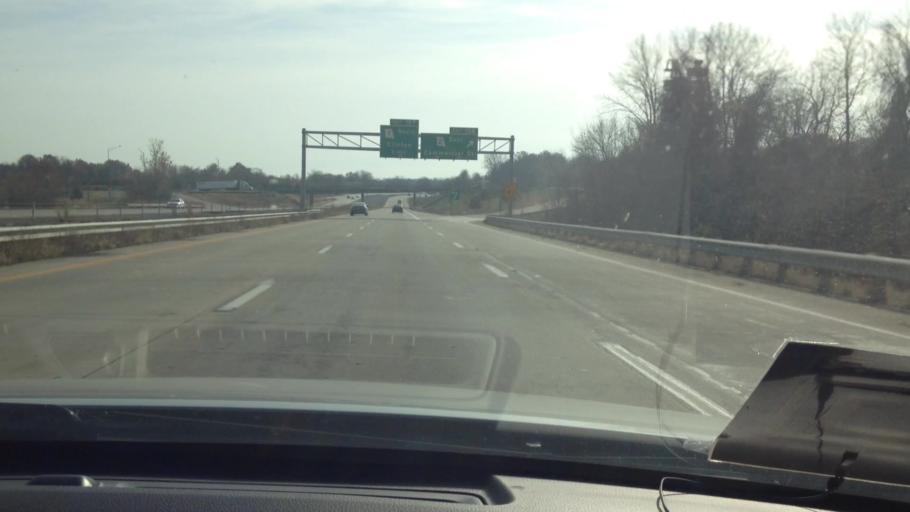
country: US
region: Missouri
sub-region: Cass County
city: Harrisonville
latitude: 38.6397
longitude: -94.3568
